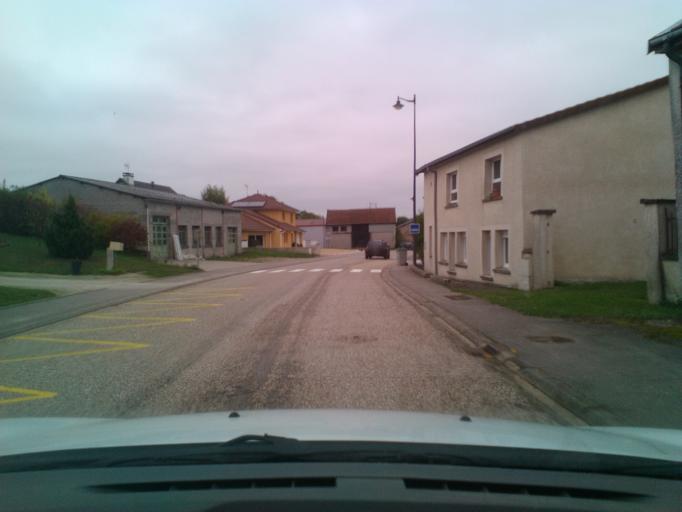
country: FR
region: Lorraine
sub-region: Departement des Vosges
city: Thaon-les-Vosges
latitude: 48.2921
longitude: 6.4447
